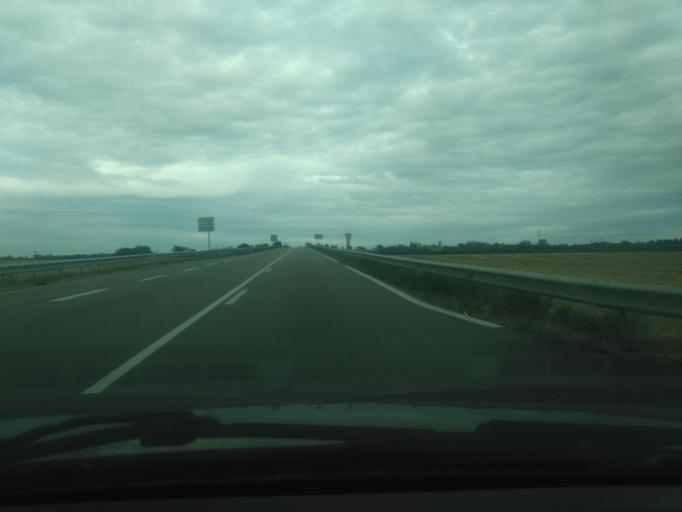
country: FR
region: Bourgogne
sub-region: Departement de la Nievre
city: Saint-Pierre-le-Moutier
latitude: 46.8022
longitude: 3.1090
